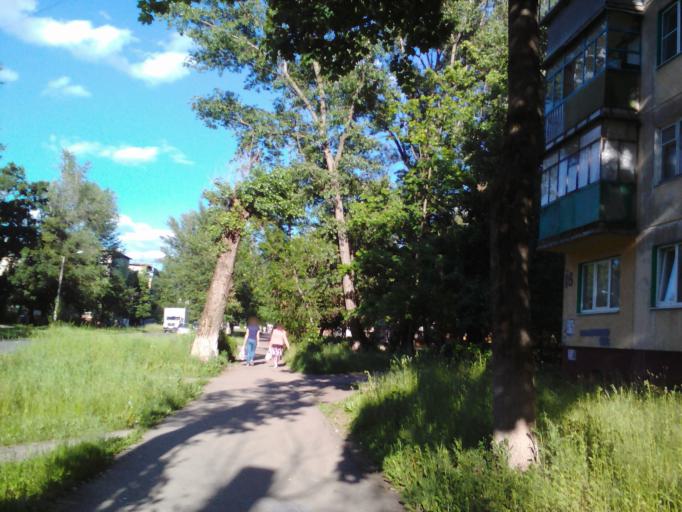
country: RU
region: Kursk
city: Voroshnevo
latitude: 51.6695
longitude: 36.0777
